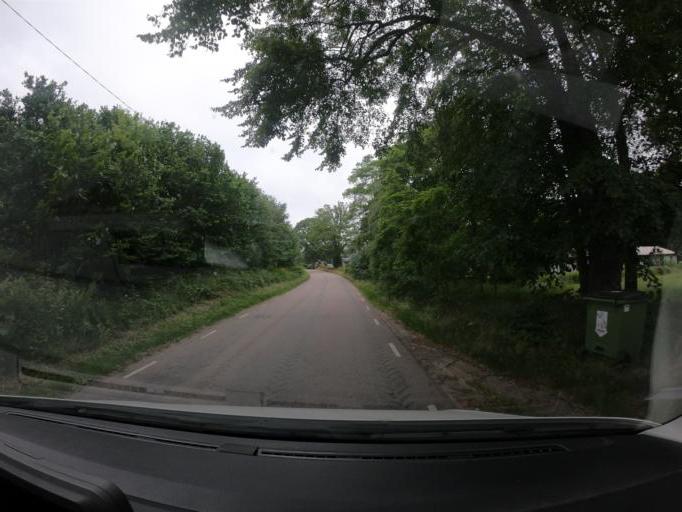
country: SE
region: Skane
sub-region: Klippans Kommun
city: Ljungbyhed
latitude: 56.0475
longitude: 13.2570
